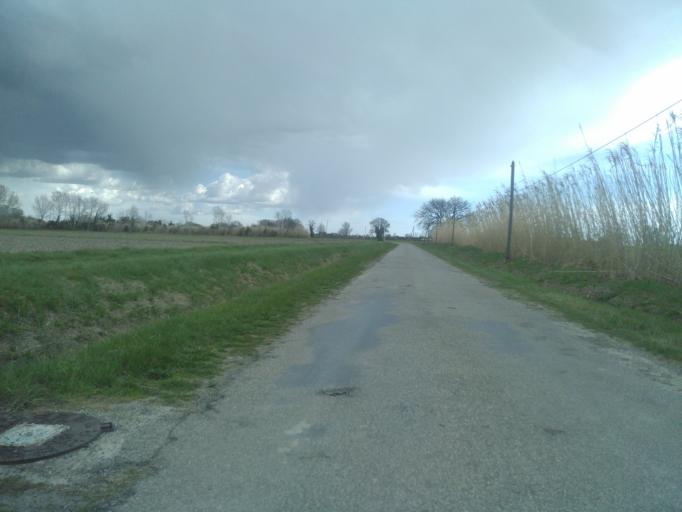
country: FR
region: Provence-Alpes-Cote d'Azur
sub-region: Departement des Bouches-du-Rhone
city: Arles
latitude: 43.6318
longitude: 4.5797
